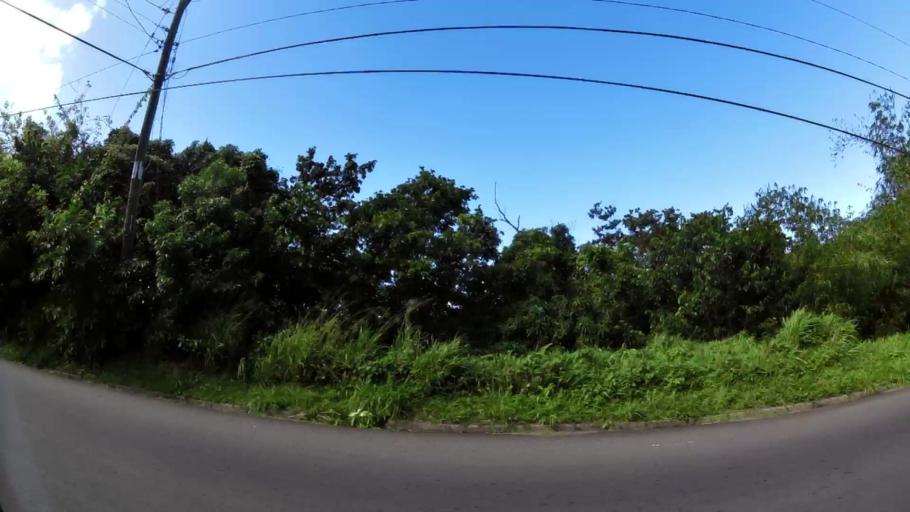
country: LC
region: Choiseul Quarter
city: Choiseul
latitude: 13.8077
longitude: -61.0378
